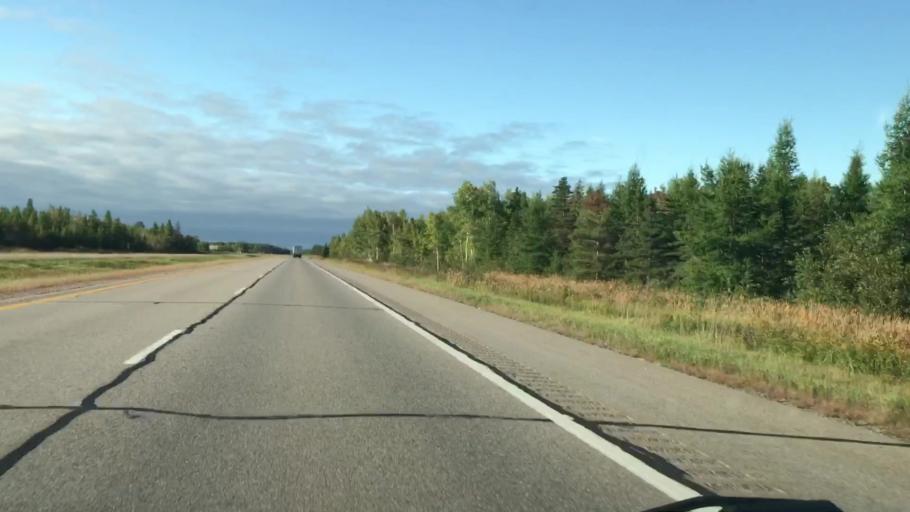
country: US
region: Michigan
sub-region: Chippewa County
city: Sault Ste. Marie
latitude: 46.4050
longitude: -84.4011
